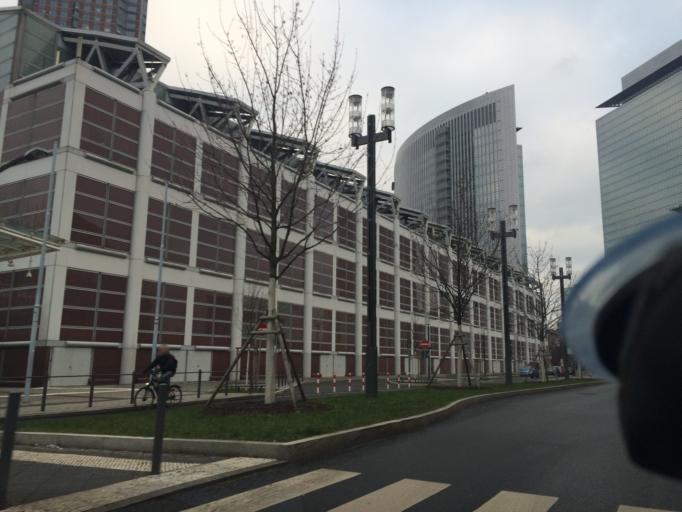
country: DE
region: Hesse
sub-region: Regierungsbezirk Darmstadt
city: Frankfurt am Main
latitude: 50.1105
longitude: 8.6515
